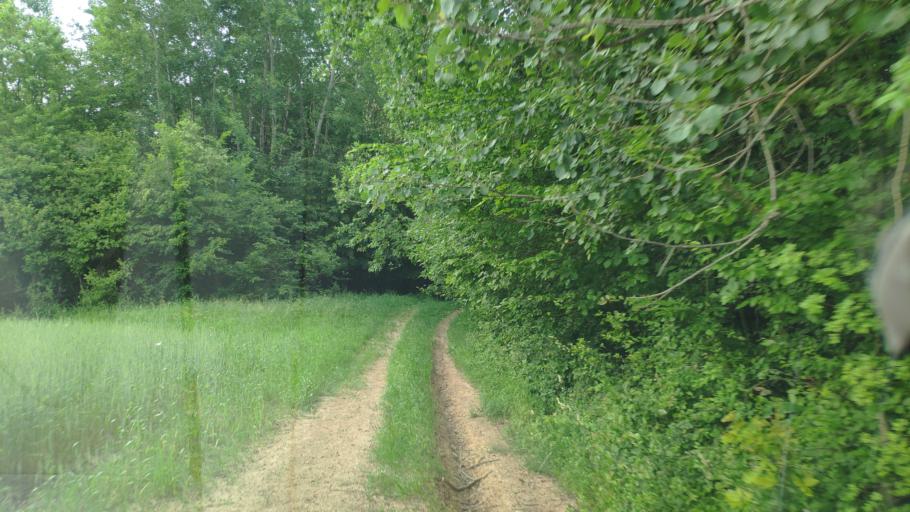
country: SK
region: Presovsky
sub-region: Okres Presov
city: Presov
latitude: 48.9575
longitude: 21.1349
